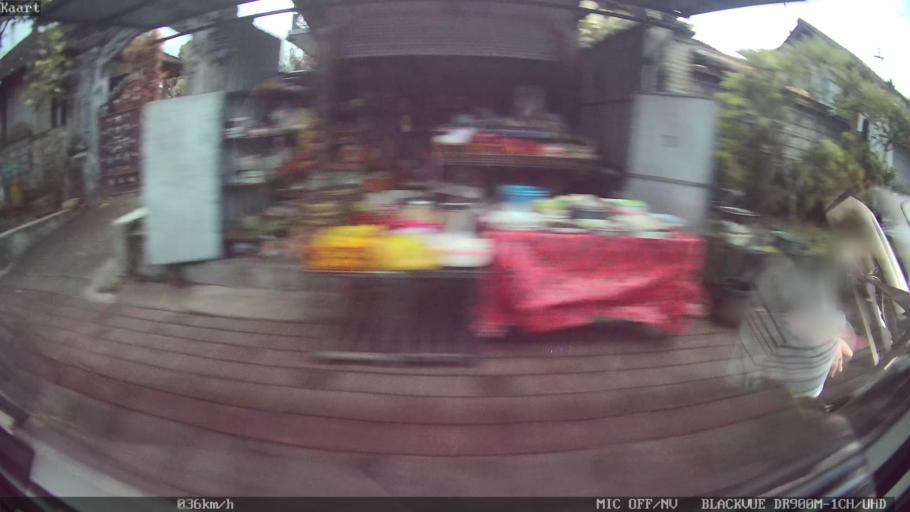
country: ID
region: Bali
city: Banjar Cemenggon
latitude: -8.5378
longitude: 115.1993
